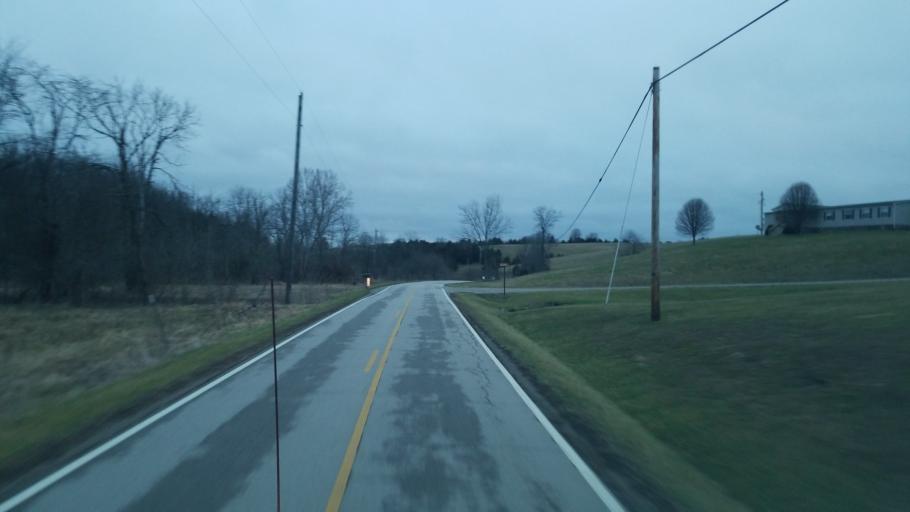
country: US
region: Kentucky
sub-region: Mason County
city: Maysville
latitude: 38.5394
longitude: -83.6943
